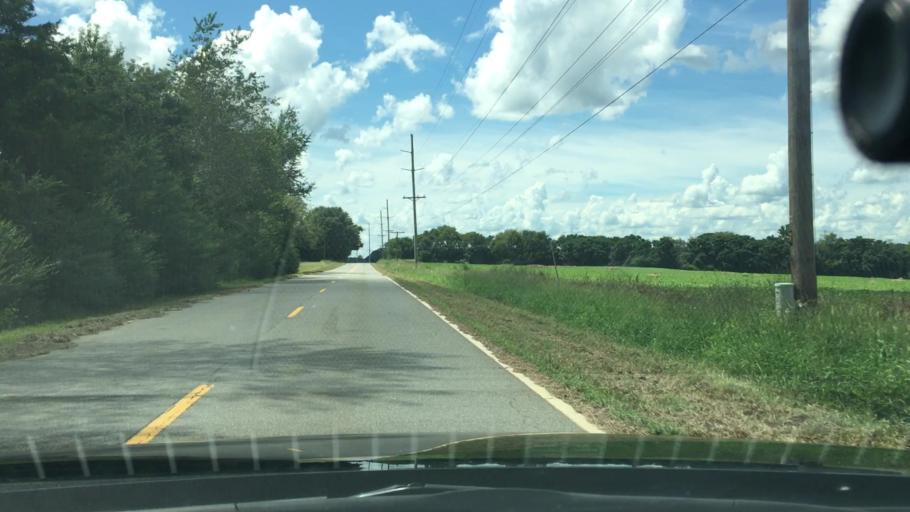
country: US
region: Georgia
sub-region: Putnam County
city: Jefferson
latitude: 33.3717
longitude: -83.2944
